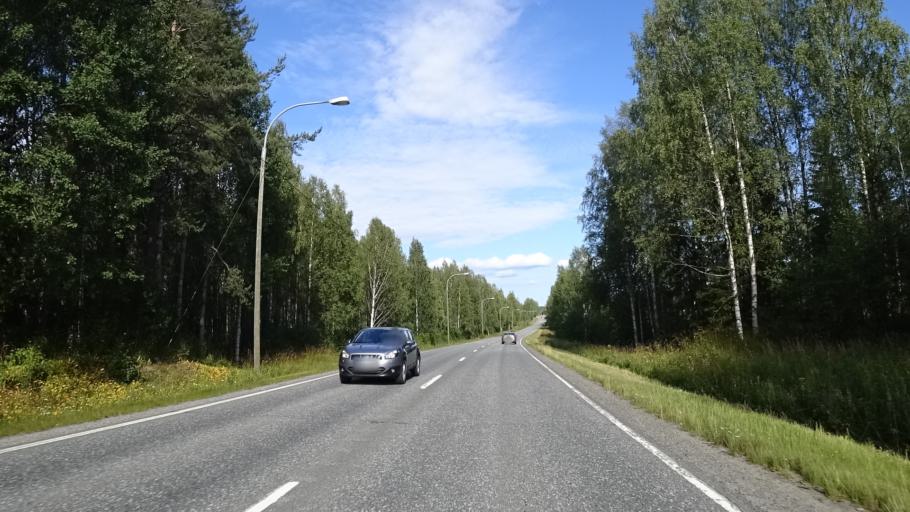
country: FI
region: North Karelia
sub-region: Joensuu
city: Eno
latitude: 62.7959
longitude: 30.0942
